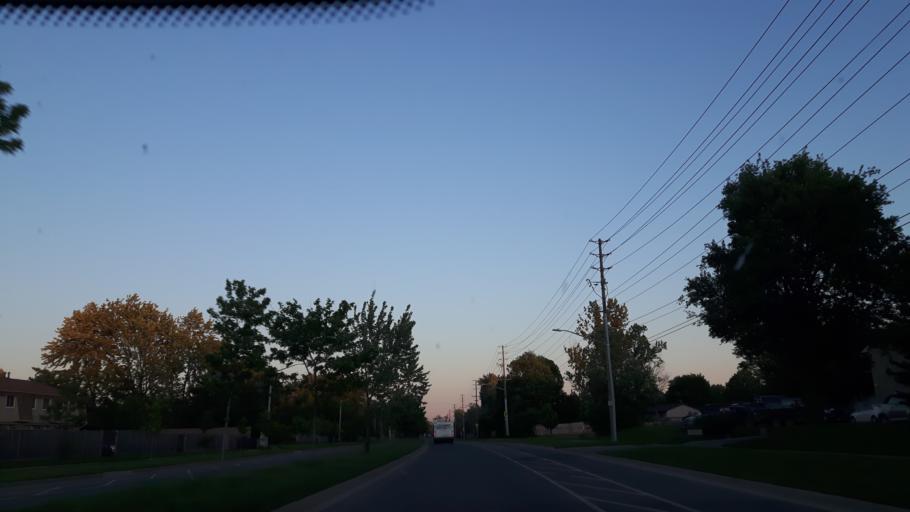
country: CA
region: Ontario
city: London
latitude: 42.9417
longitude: -81.2129
